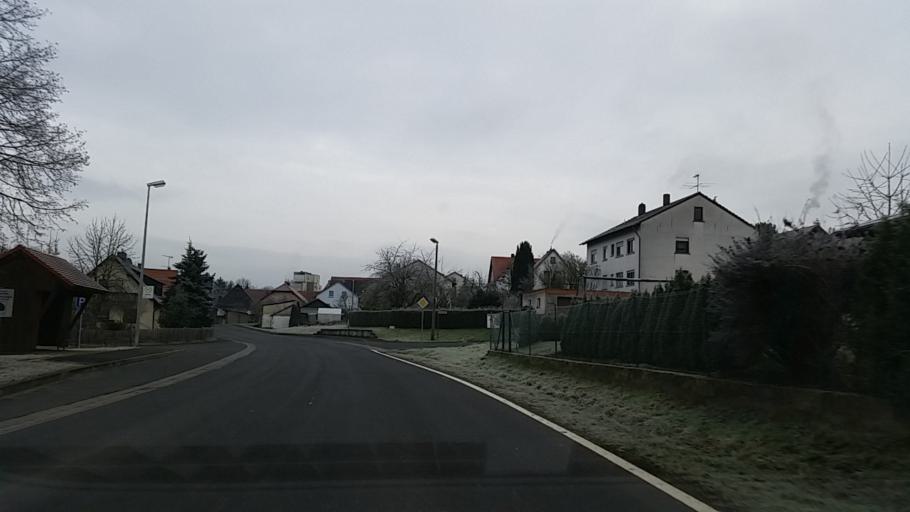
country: DE
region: Bavaria
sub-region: Regierungsbezirk Unterfranken
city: Eussenheim
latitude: 50.0144
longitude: 9.8760
